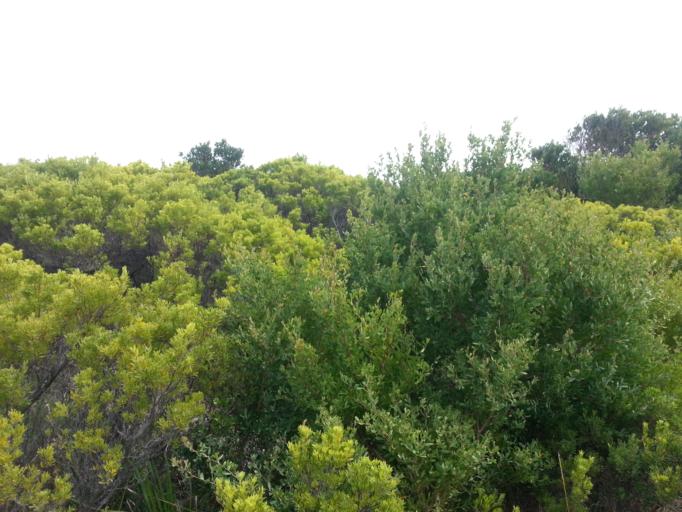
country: AU
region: Victoria
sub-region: Colac-Otway
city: Apollo Bay
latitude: -38.8548
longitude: 143.5231
